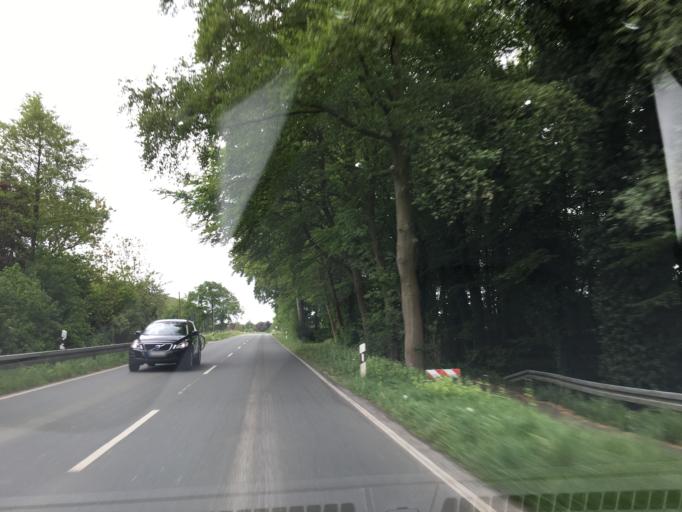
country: DE
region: North Rhine-Westphalia
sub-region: Regierungsbezirk Munster
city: Havixbeck
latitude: 51.9383
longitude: 7.4497
